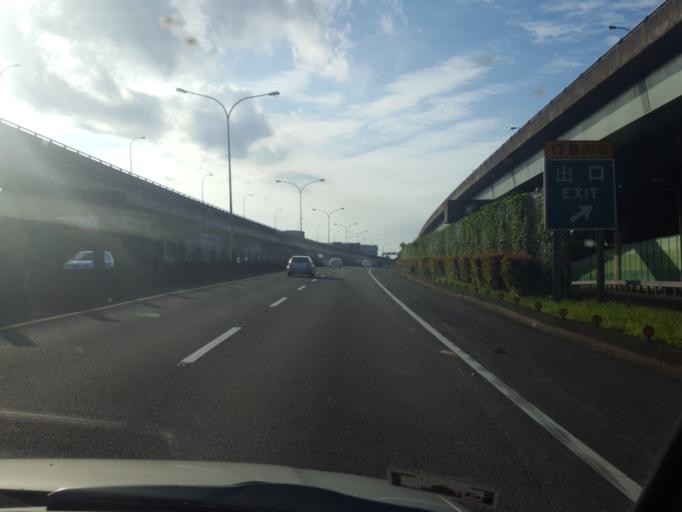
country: TW
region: Taipei
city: Taipei
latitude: 25.0642
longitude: 121.5931
